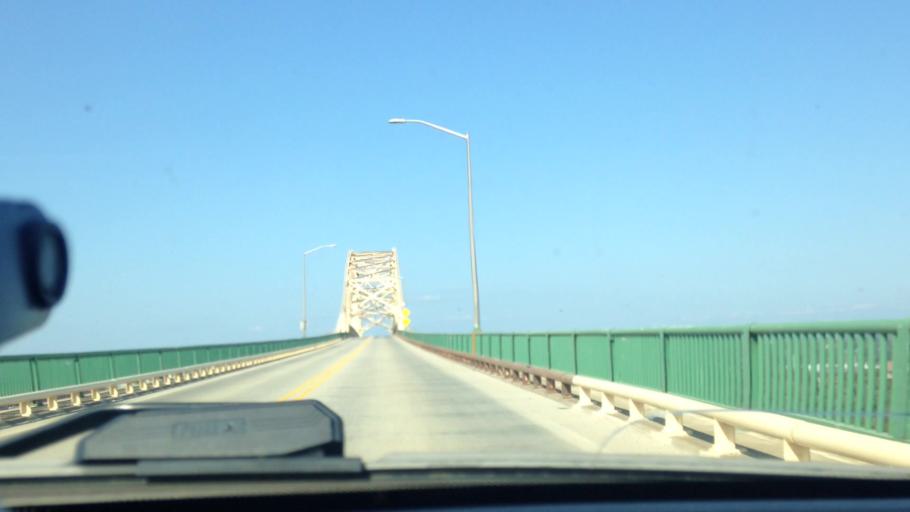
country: US
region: Michigan
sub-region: Chippewa County
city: Sault Ste. Marie
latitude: 46.5105
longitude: -84.3599
